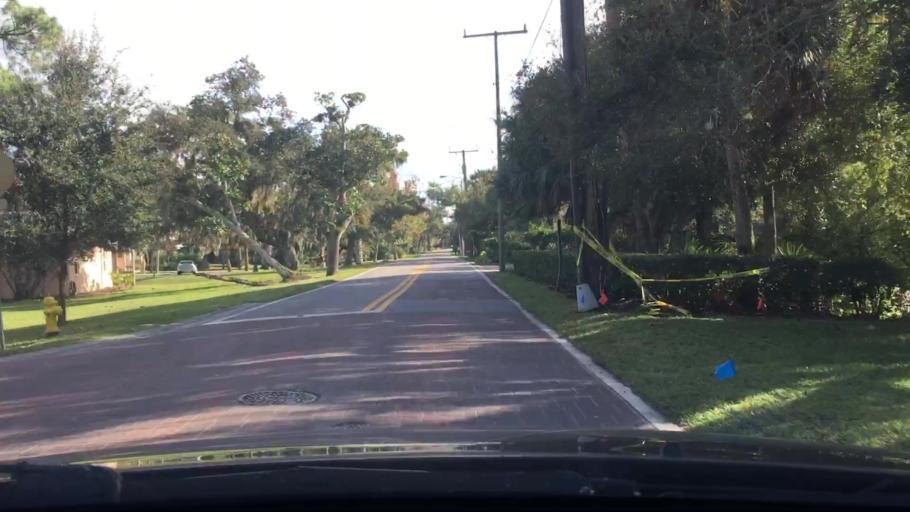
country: US
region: Florida
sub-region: Volusia County
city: Ormond Beach
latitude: 29.3091
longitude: -81.0569
